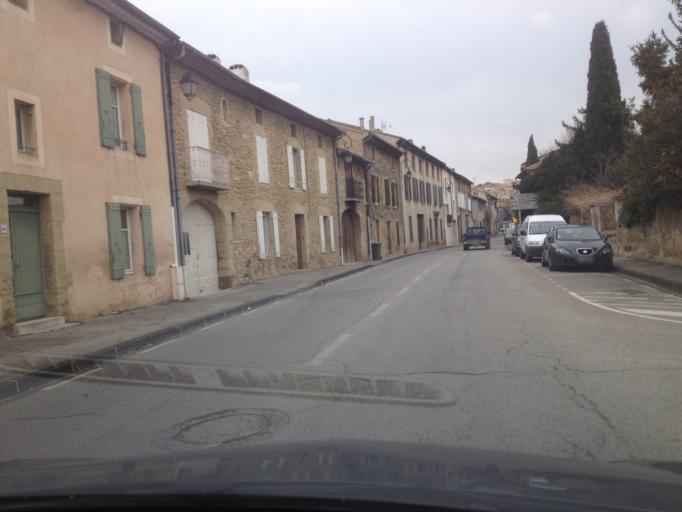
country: FR
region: Provence-Alpes-Cote d'Azur
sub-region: Departement du Vaucluse
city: Courthezon
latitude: 44.0840
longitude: 4.8815
